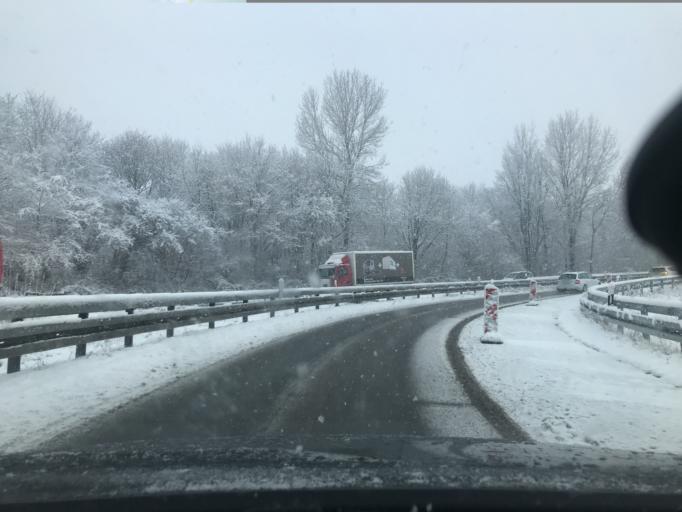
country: DE
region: North Rhine-Westphalia
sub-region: Regierungsbezirk Koln
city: Leverkusen
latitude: 51.0235
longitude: 6.9400
